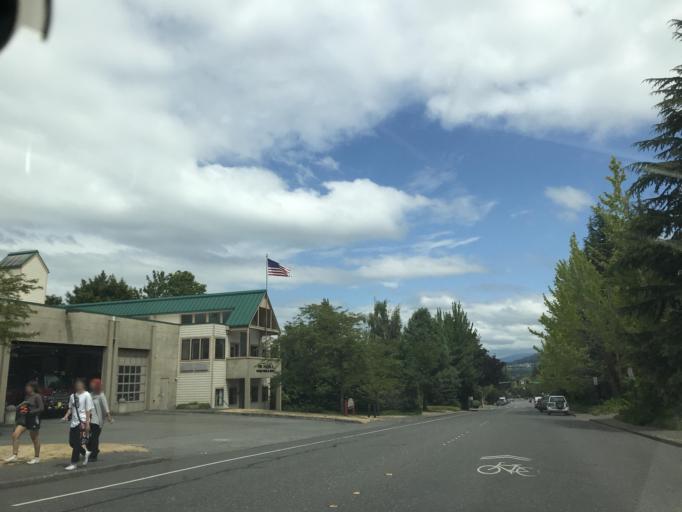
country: US
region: Washington
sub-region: Whatcom County
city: Bellingham
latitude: 48.7437
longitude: -122.4759
